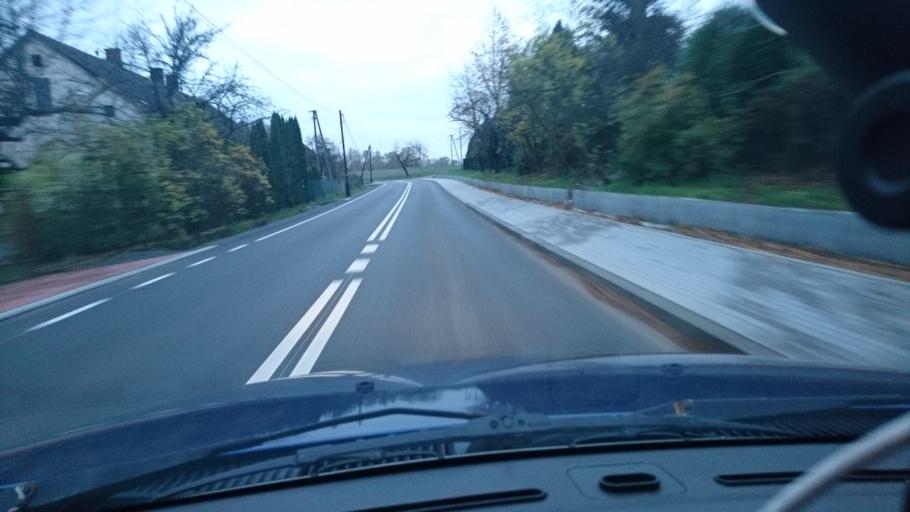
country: PL
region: Silesian Voivodeship
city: Janowice
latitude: 49.9076
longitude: 19.0883
